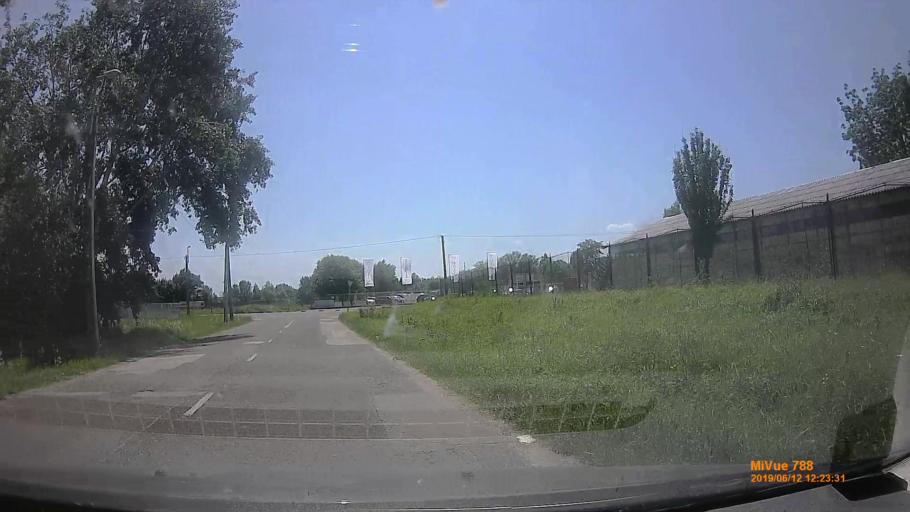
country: HU
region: Bacs-Kiskun
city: Kecskemet
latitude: 46.8918
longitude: 19.7013
